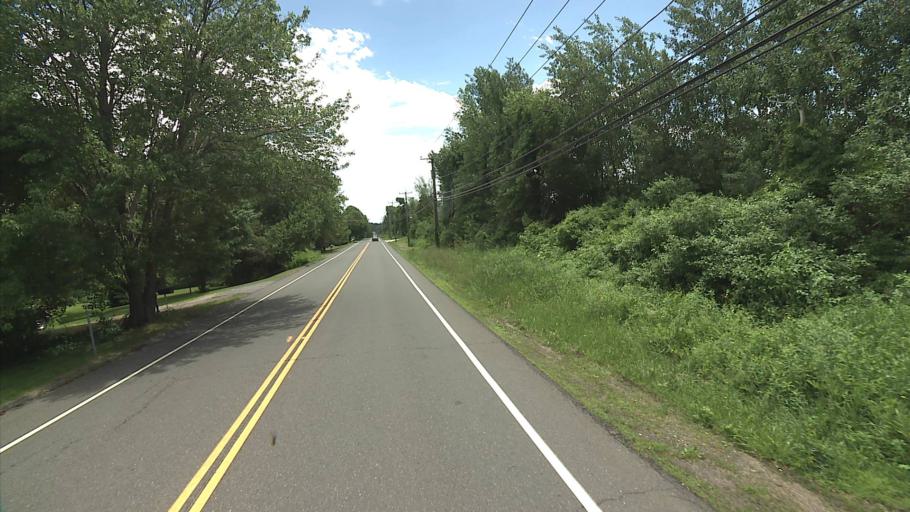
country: US
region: Connecticut
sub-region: Litchfield County
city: Watertown
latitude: 41.6396
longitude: -73.1441
